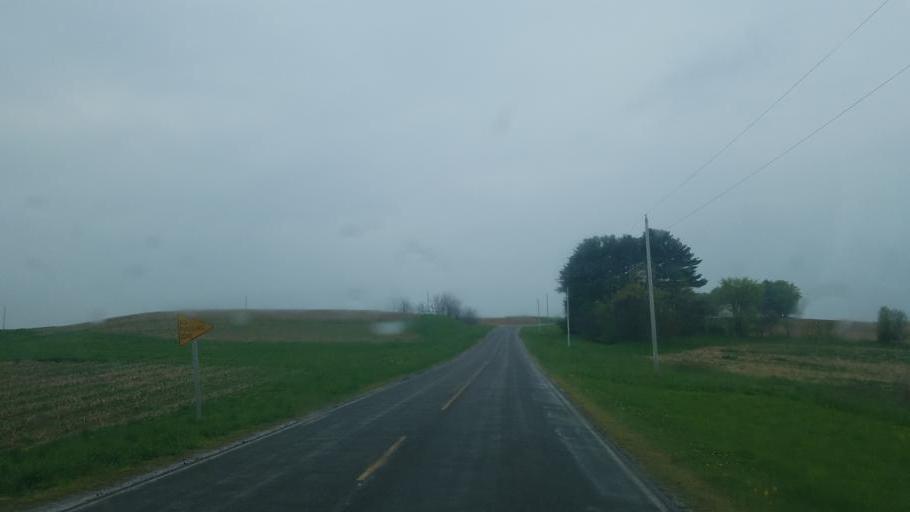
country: US
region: Wisconsin
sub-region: Vernon County
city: Hillsboro
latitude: 43.6498
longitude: -90.2542
